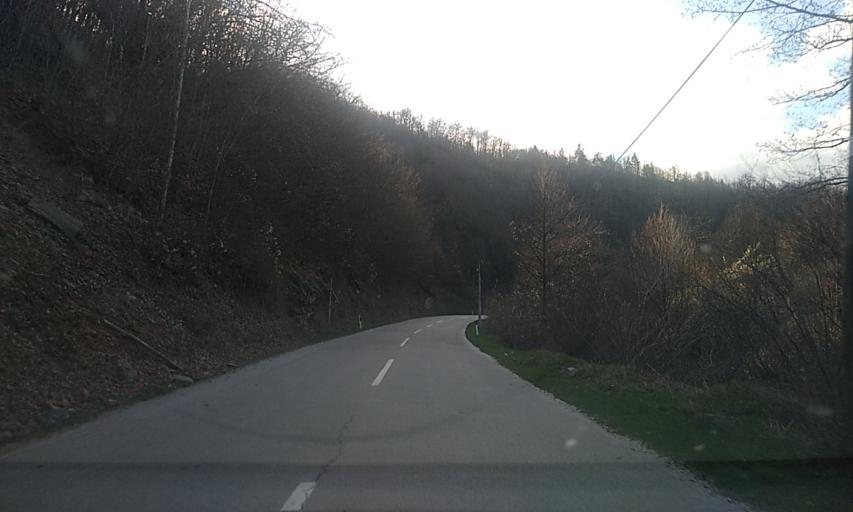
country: RS
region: Central Serbia
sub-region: Pcinjski Okrug
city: Bosilegrad
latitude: 42.4314
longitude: 22.5143
